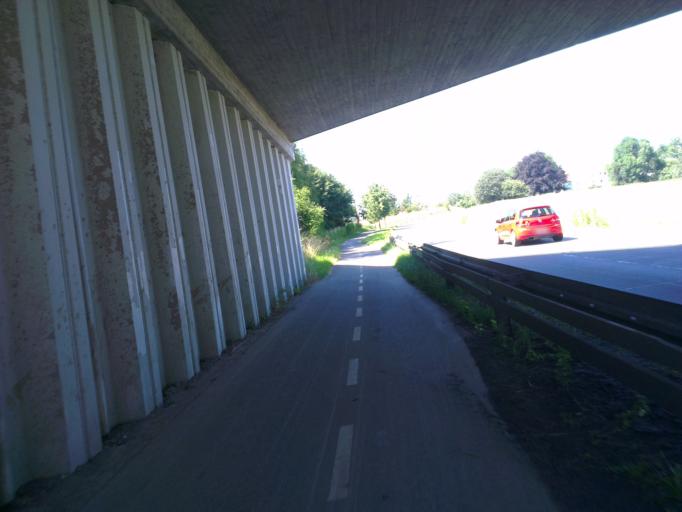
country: DK
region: Capital Region
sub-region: Frederikssund Kommune
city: Slangerup
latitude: 55.8351
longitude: 12.1830
